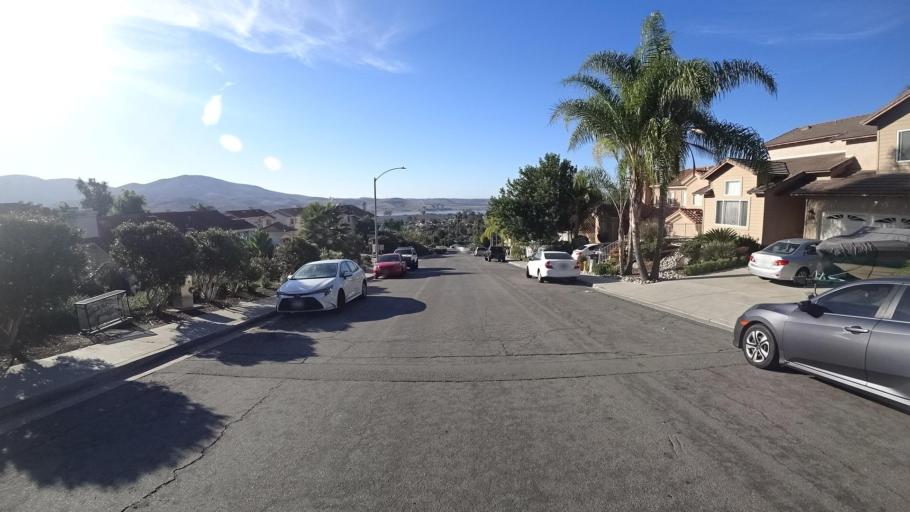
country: US
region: California
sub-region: San Diego County
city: La Presa
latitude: 32.7138
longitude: -116.9888
